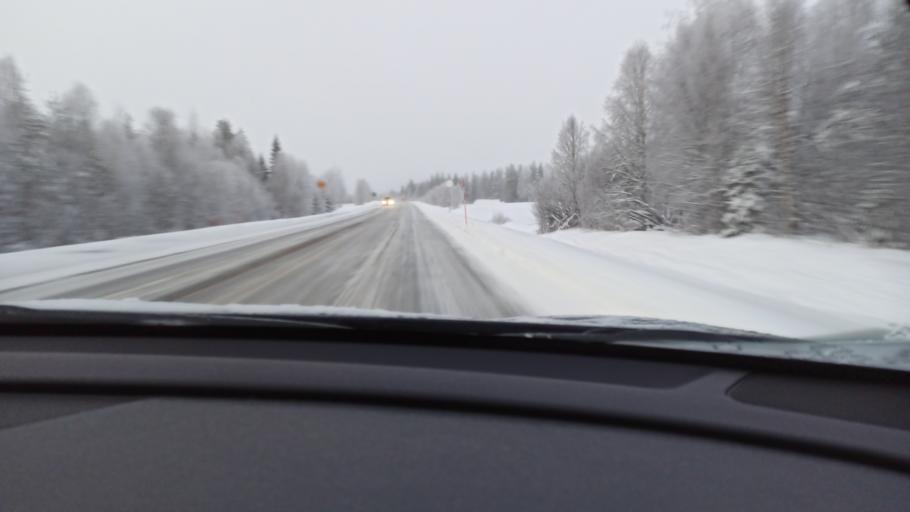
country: FI
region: Lapland
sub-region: Pohjois-Lappi
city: Sodankylae
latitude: 66.9290
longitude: 26.2422
